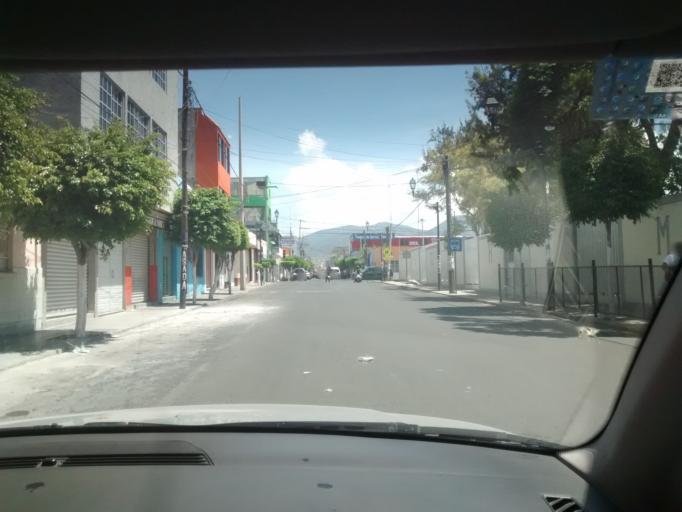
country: MX
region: Puebla
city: Tehuacan
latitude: 18.4559
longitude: -97.3916
